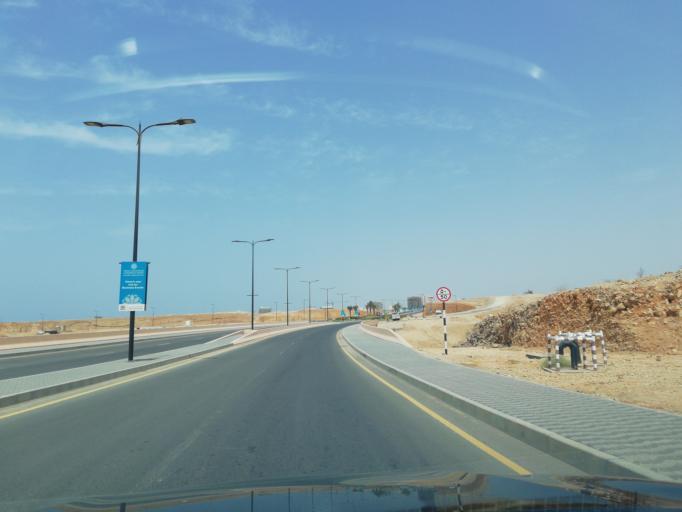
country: OM
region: Muhafazat Masqat
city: Bawshar
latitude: 23.5773
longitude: 58.3257
